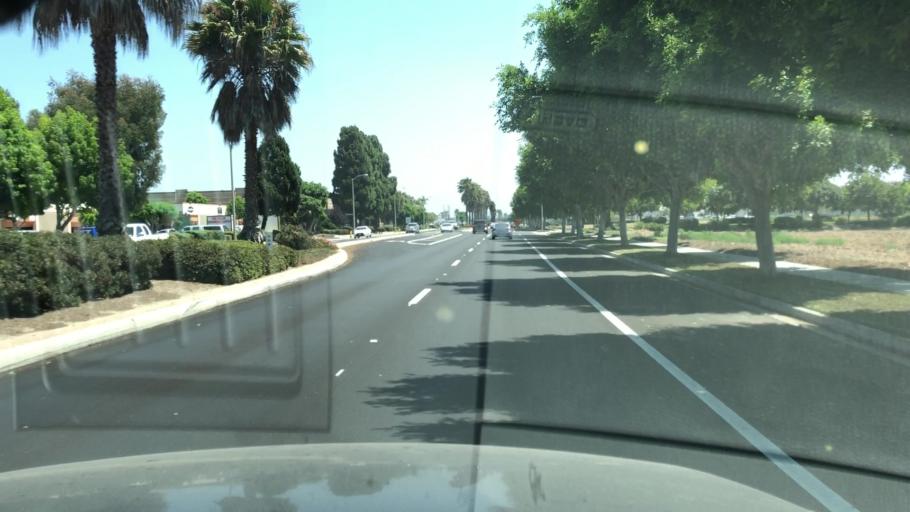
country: US
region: California
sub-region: Ventura County
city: Oxnard Shores
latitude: 34.1975
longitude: -119.2159
